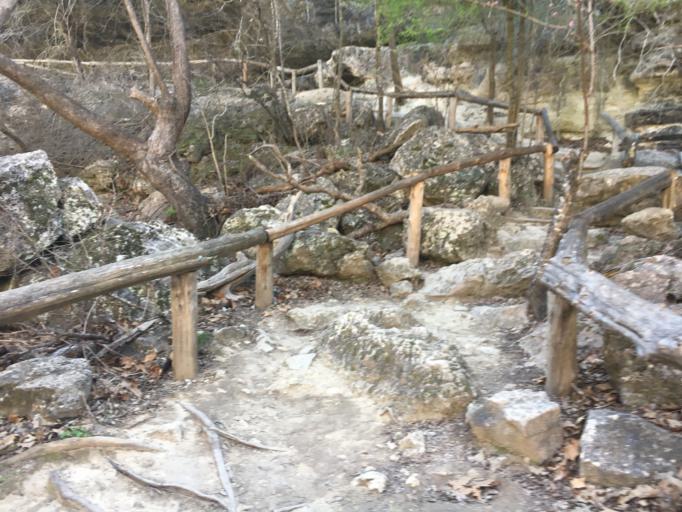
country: US
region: Texas
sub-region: Travis County
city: Briarcliff
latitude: 30.3423
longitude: -98.1272
